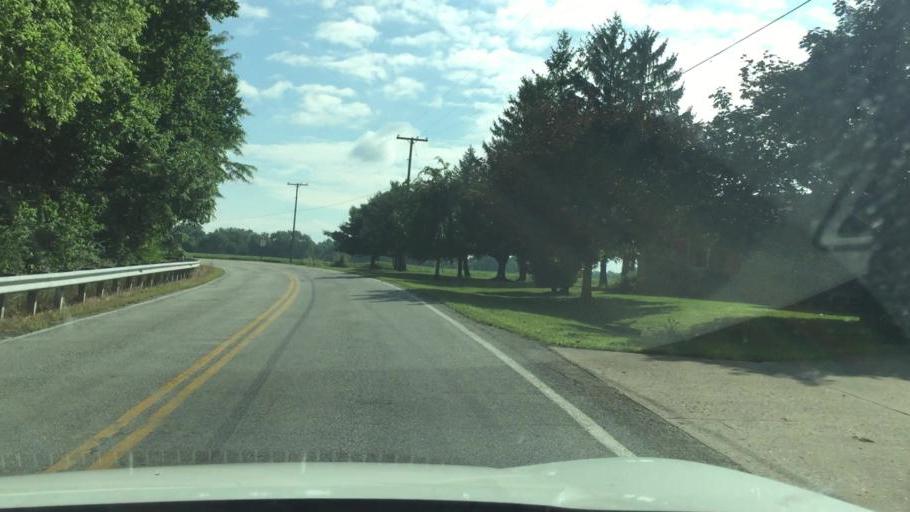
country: US
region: Ohio
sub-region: Clark County
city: Northridge
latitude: 39.9988
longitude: -83.7131
